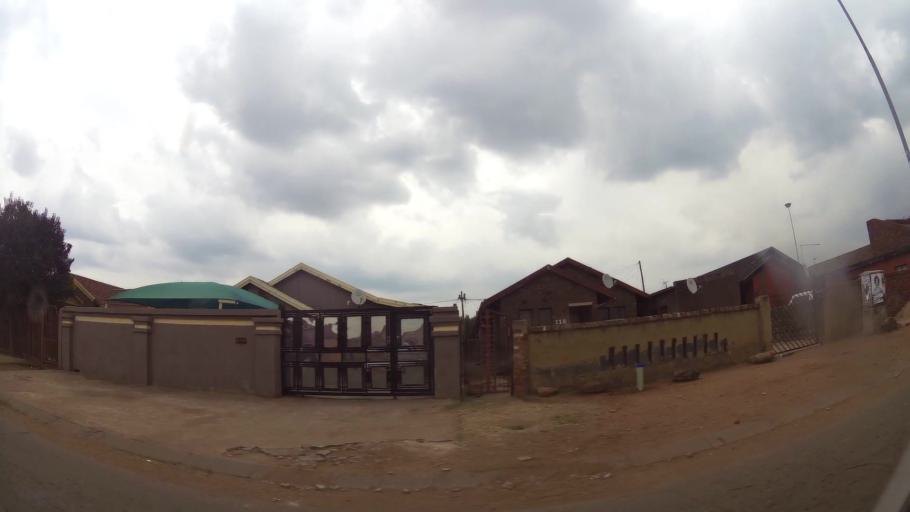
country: ZA
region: Gauteng
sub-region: Ekurhuleni Metropolitan Municipality
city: Germiston
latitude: -26.3603
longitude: 28.1499
